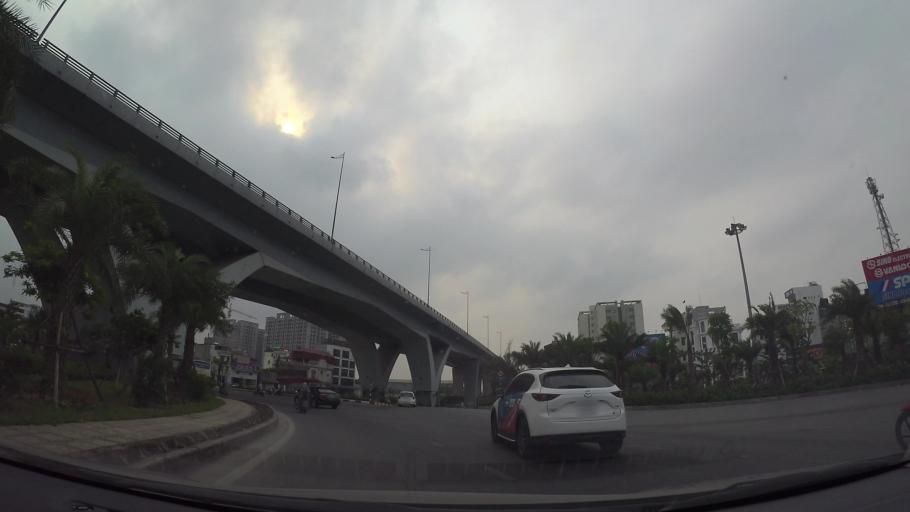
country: VN
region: Ha Noi
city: Hoan Kiem
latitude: 21.0555
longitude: 105.8883
